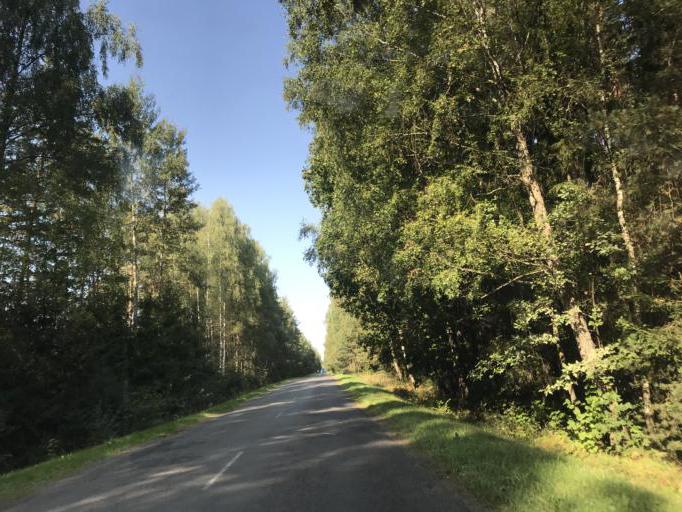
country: BY
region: Mogilev
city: Myazhysyatki
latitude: 53.8010
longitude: 30.1741
